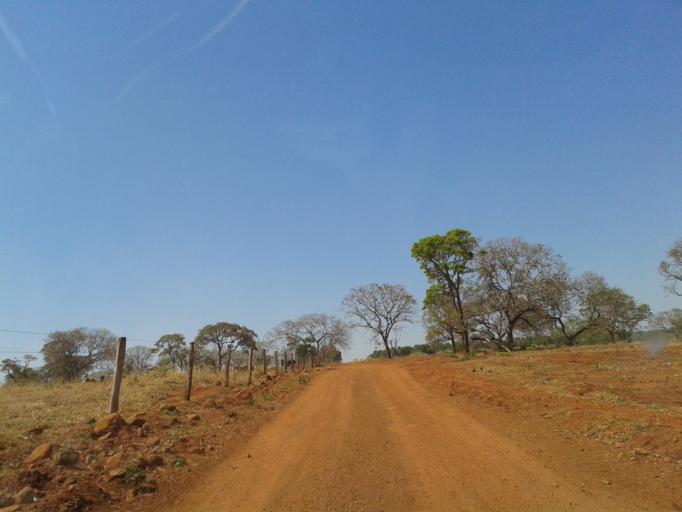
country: BR
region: Minas Gerais
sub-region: Ituiutaba
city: Ituiutaba
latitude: -19.0519
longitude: -49.3774
